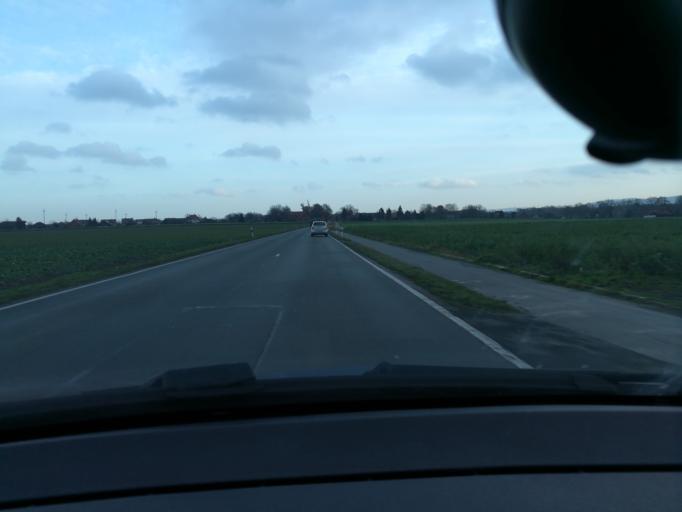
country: DE
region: North Rhine-Westphalia
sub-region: Regierungsbezirk Detmold
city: Hille
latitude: 52.3177
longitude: 8.8065
